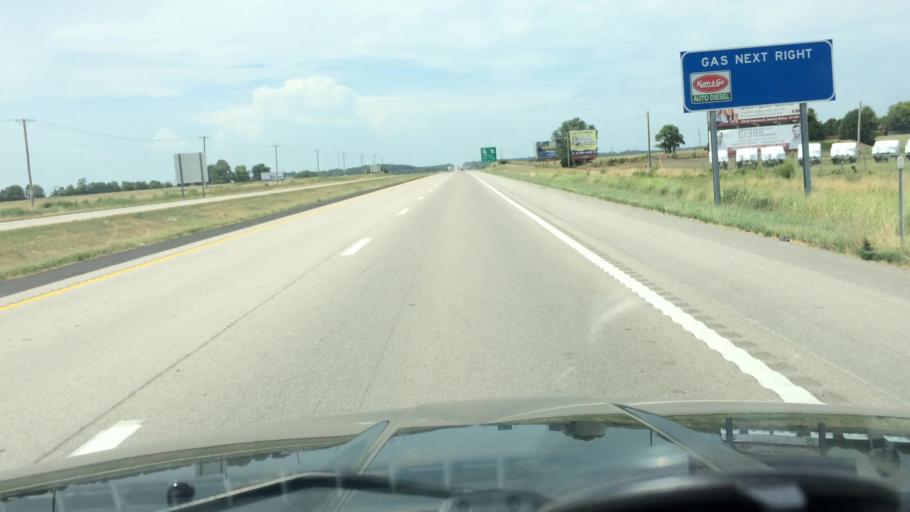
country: US
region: Missouri
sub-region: Polk County
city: Bolivar
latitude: 37.6013
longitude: -93.4387
